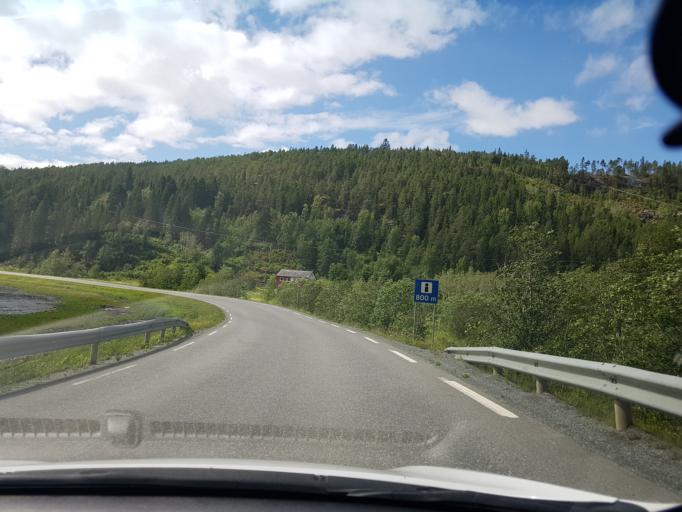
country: NO
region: Nord-Trondelag
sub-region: Stjordal
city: Stjordal
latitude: 63.6157
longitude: 10.9135
